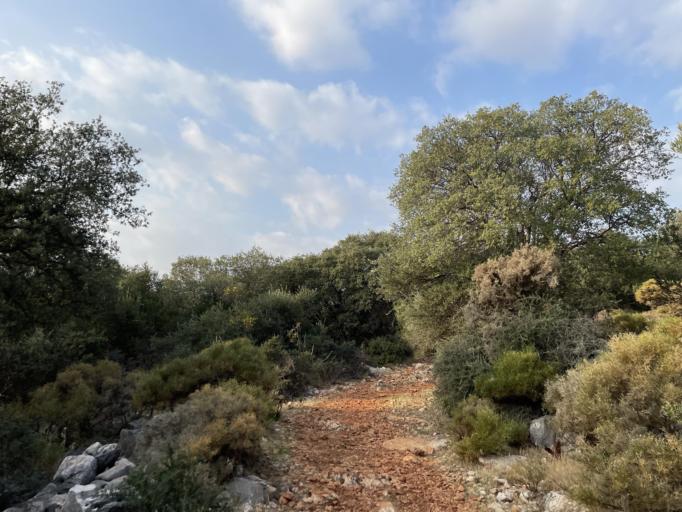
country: TR
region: Antalya
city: Kas
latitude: 36.1619
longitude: 29.6554
